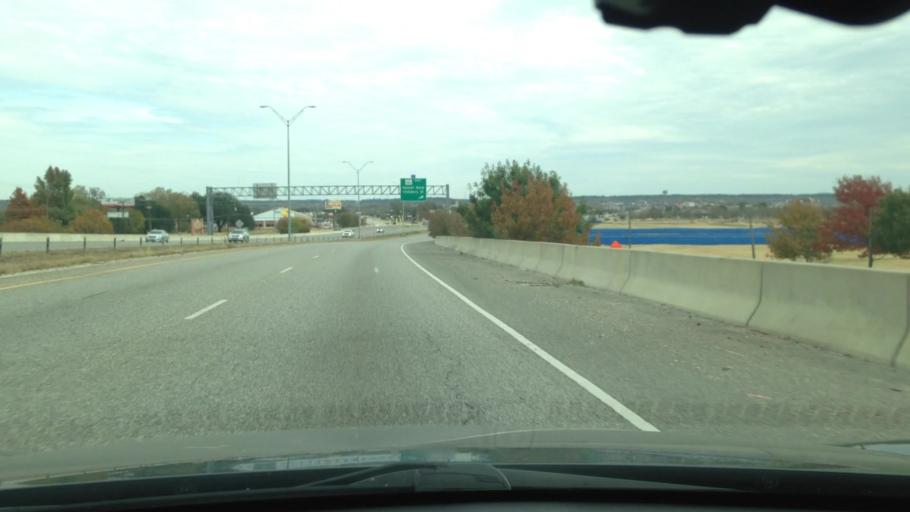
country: US
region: Texas
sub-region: Bastrop County
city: Bastrop
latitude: 30.1111
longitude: -97.3492
